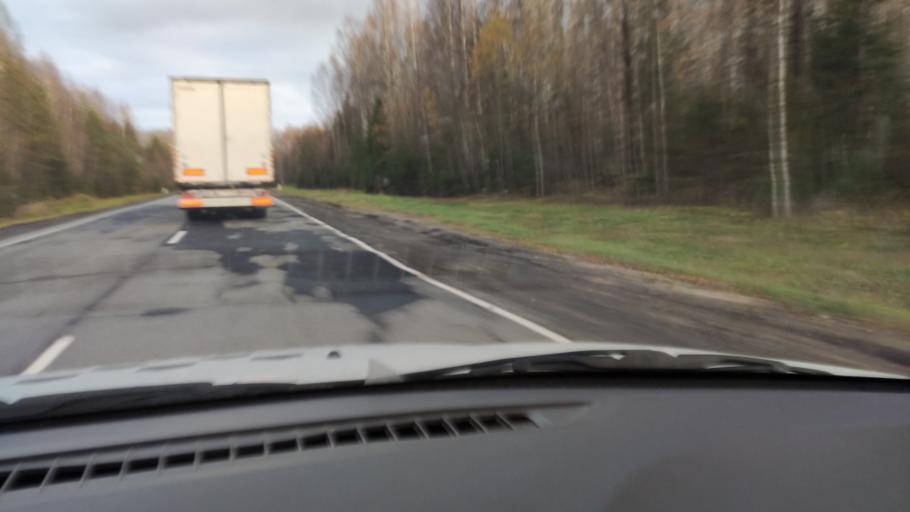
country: RU
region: Kirov
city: Chernaya Kholunitsa
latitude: 58.7717
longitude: 51.9501
